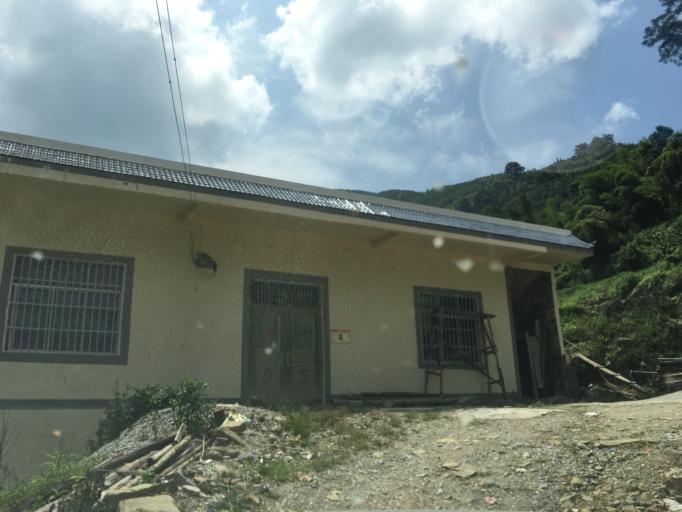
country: CN
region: Guangxi Zhuangzu Zizhiqu
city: Xinzhou
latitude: 24.9548
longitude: 105.7841
